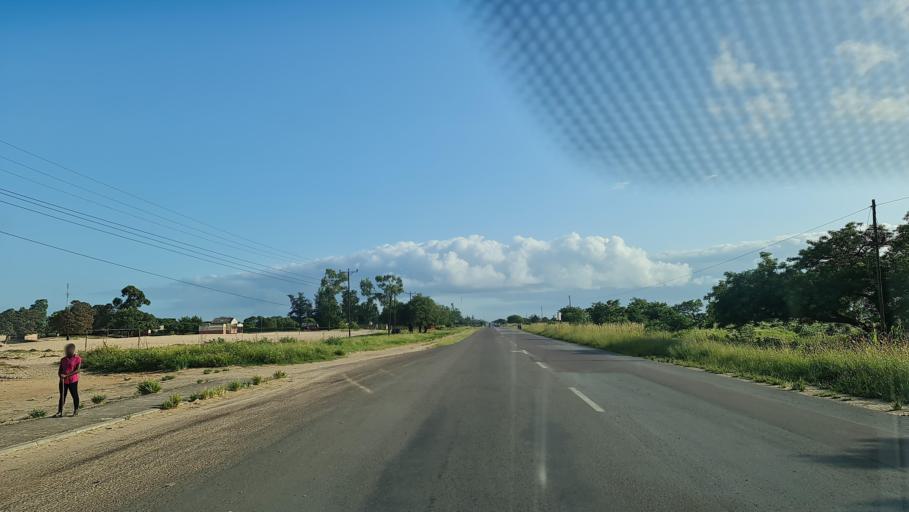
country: MZ
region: Maputo City
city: Maputo
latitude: -25.6824
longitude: 32.6660
